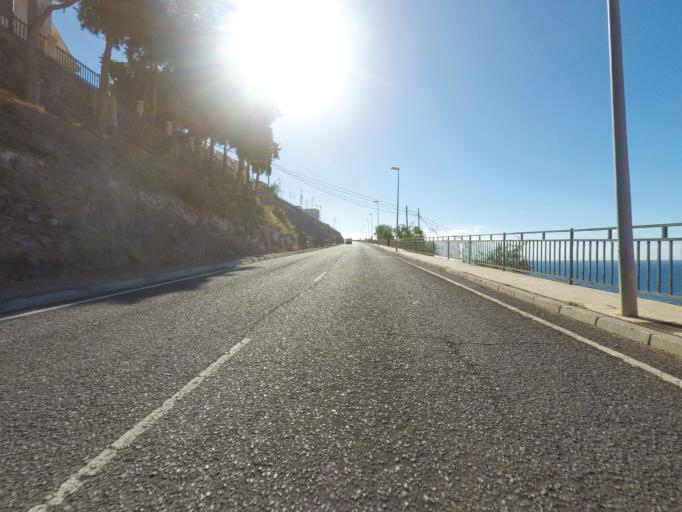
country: ES
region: Canary Islands
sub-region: Provincia de Santa Cruz de Tenerife
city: Alajero
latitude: 28.0330
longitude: -17.1923
